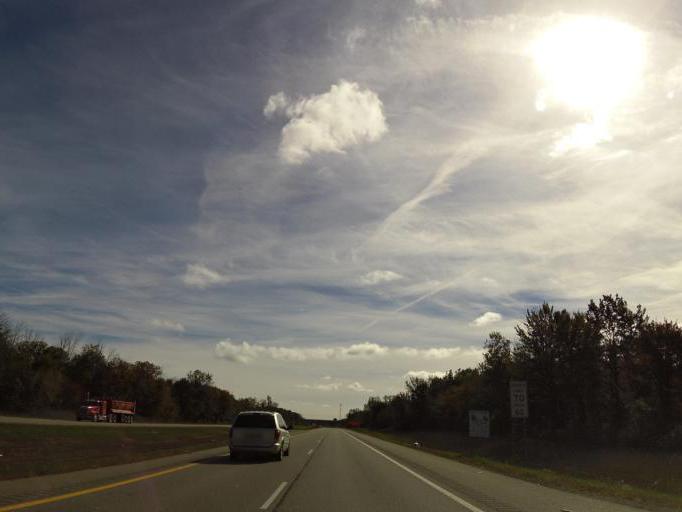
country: US
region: Michigan
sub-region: Saint Clair County
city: Marysville
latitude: 42.9757
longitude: -82.5295
